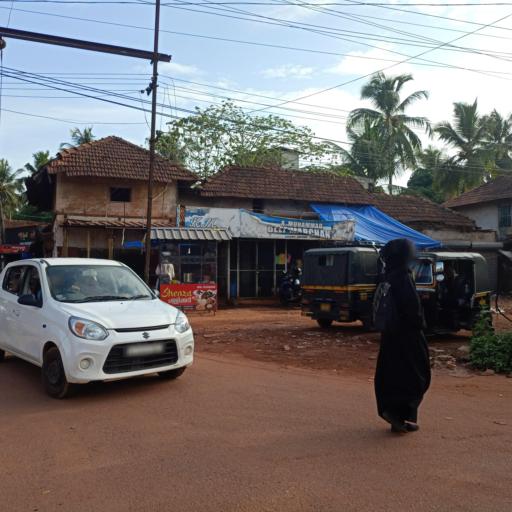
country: IN
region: Kerala
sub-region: Kasaragod District
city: Kasaragod
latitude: 12.5152
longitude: 75.0232
